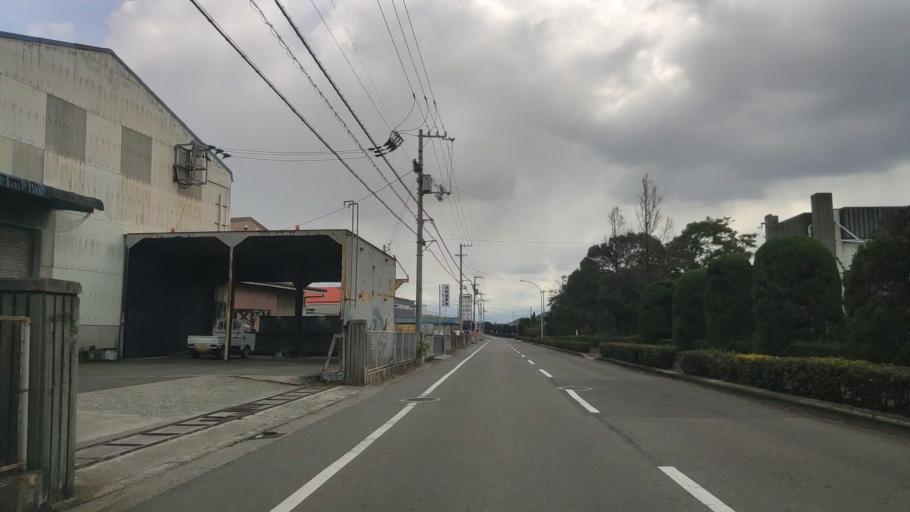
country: JP
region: Ehime
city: Saijo
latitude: 34.0547
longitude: 133.0219
